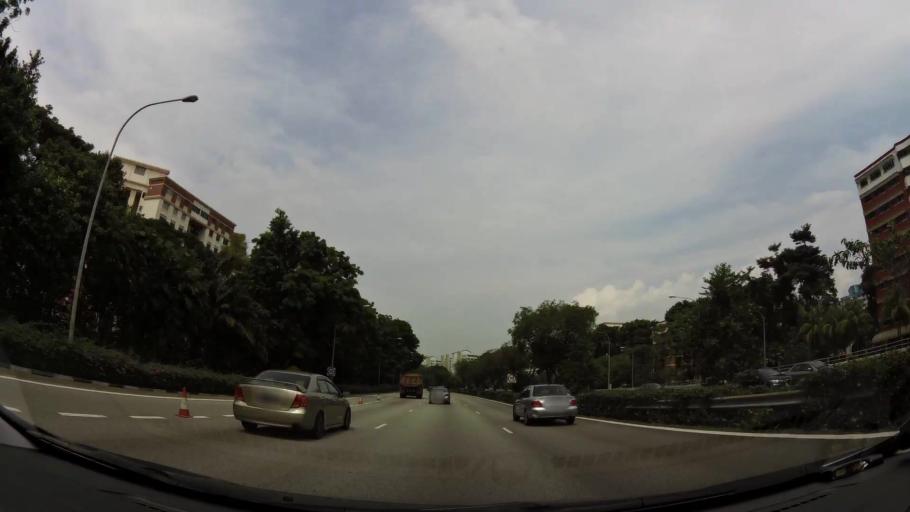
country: SG
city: Singapore
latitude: 1.3631
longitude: 103.9583
